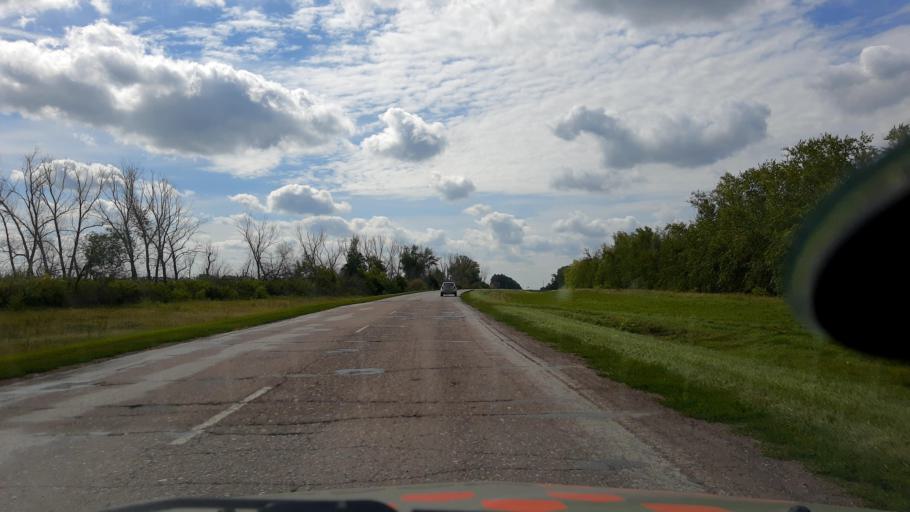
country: RU
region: Bashkortostan
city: Buzdyak
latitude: 54.7169
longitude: 54.5691
